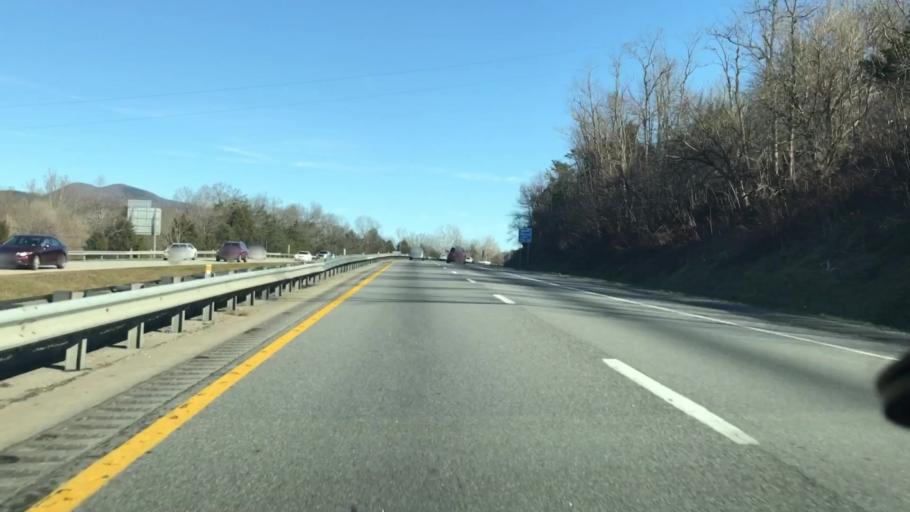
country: US
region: Virginia
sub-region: Botetourt County
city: Buchanan
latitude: 37.5598
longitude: -79.6578
